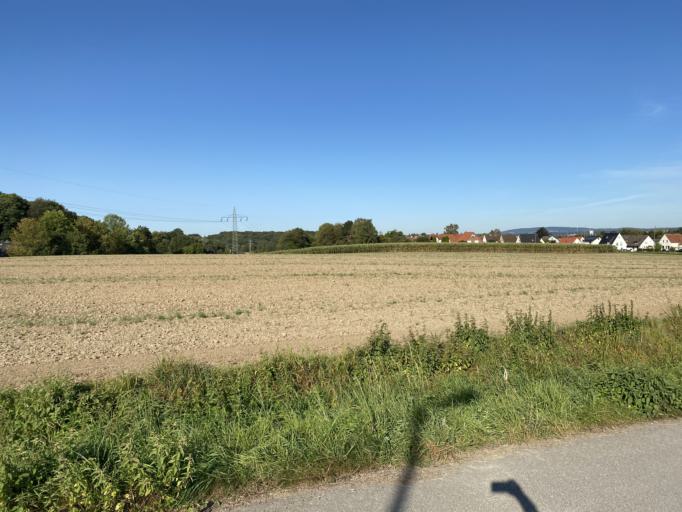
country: DE
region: North Rhine-Westphalia
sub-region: Regierungsbezirk Detmold
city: Kirchlengern
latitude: 52.1838
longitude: 8.6363
